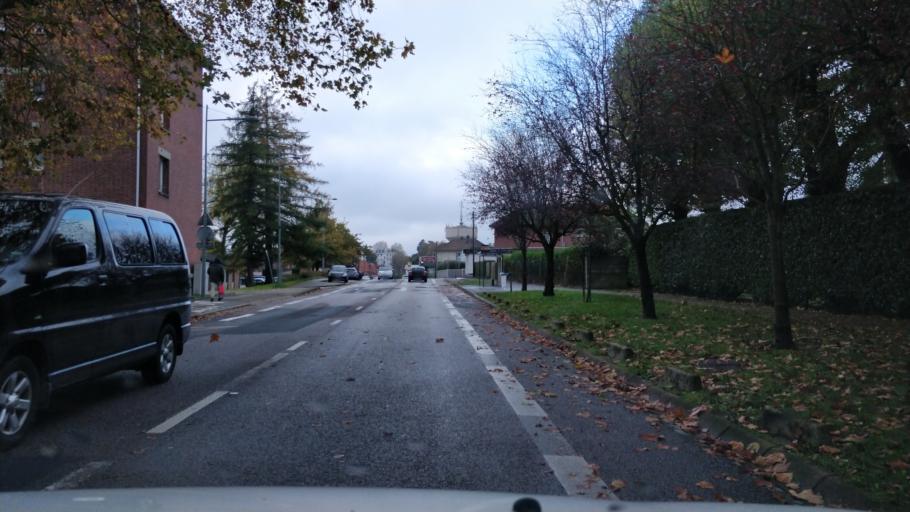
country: FR
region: Haute-Normandie
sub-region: Departement de la Seine-Maritime
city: Bihorel
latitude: 49.4564
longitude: 1.1259
